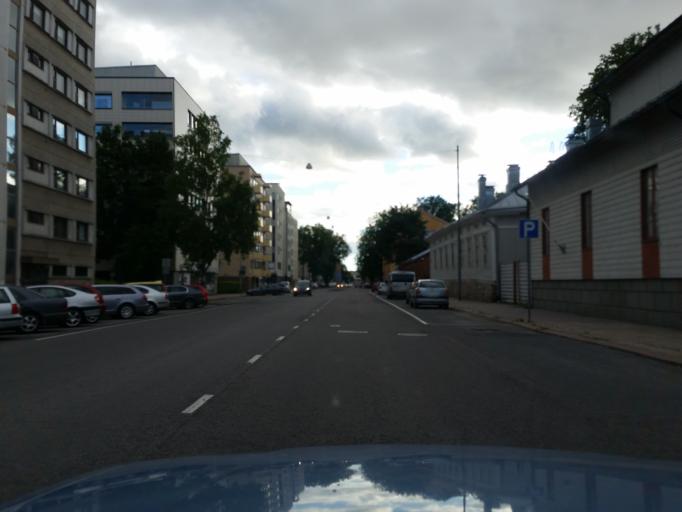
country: FI
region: Varsinais-Suomi
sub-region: Turku
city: Turku
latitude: 60.4462
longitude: 22.2828
